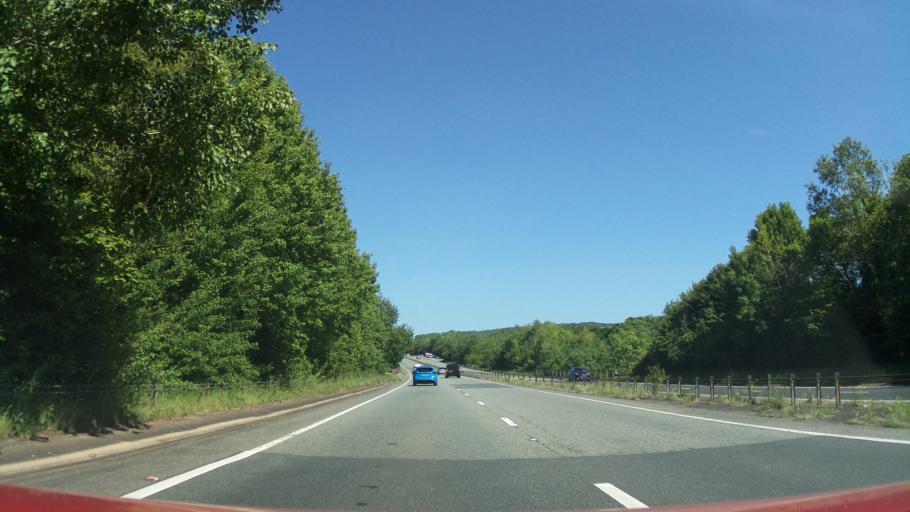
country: GB
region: England
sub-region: Devon
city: Ottery St Mary
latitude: 50.7826
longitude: -3.2582
